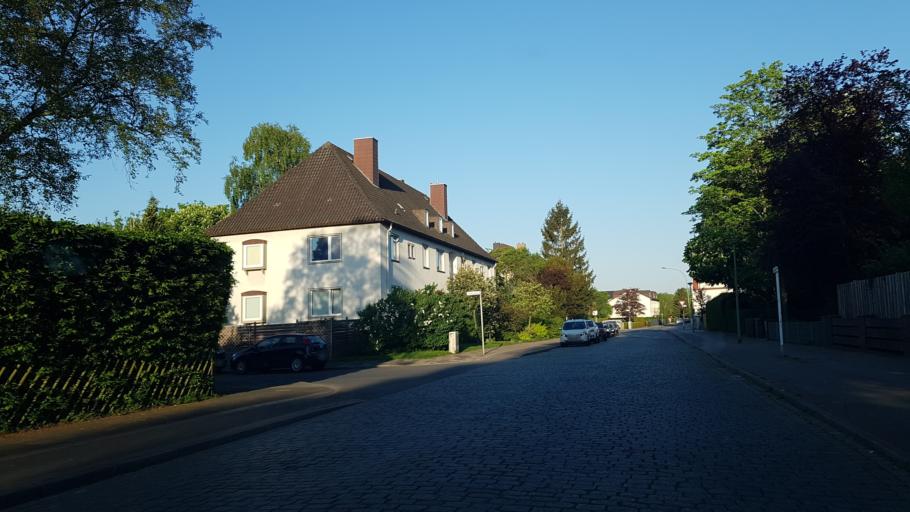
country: DE
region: Lower Saxony
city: Langen
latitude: 53.5795
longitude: 8.5938
